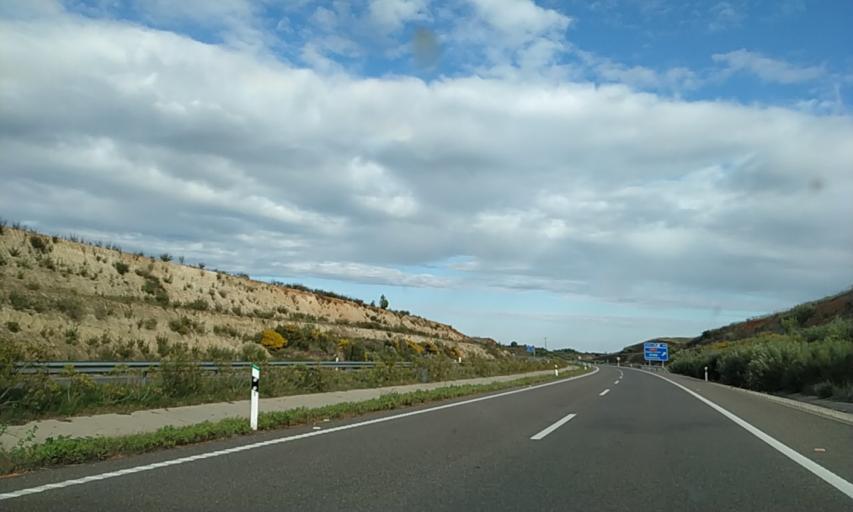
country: ES
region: Extremadura
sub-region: Provincia de Caceres
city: Casas de Don Gomez
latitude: 40.0137
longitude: -6.5807
